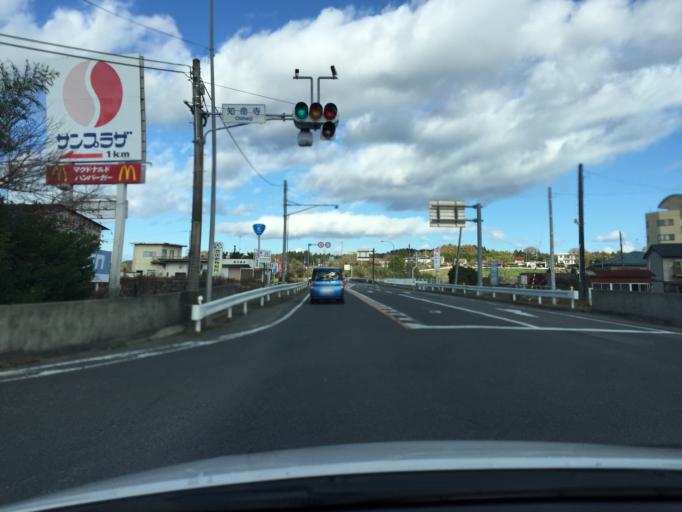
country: JP
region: Fukushima
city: Namie
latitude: 37.4955
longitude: 141.0017
